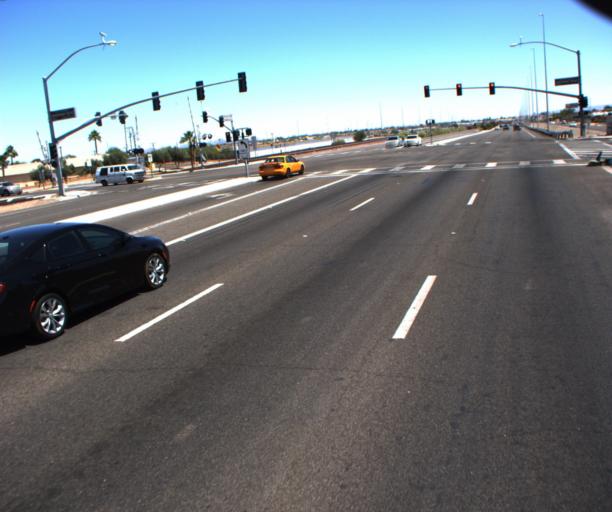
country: US
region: Arizona
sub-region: Maricopa County
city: Surprise
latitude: 33.6239
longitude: -112.3314
